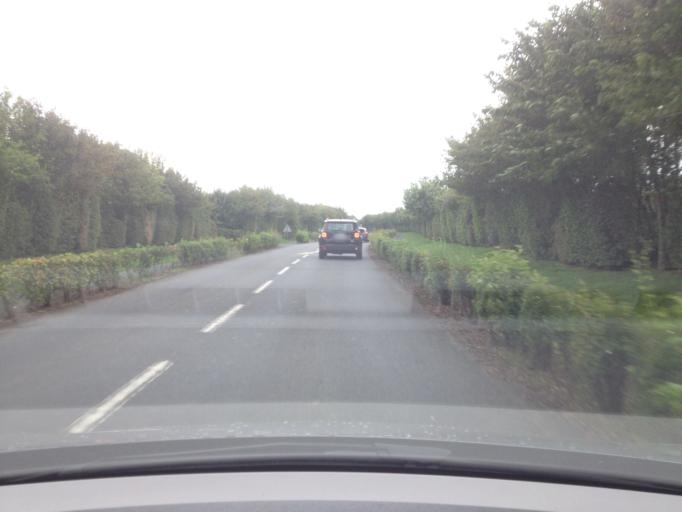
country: FR
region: Lower Normandy
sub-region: Departement du Calvados
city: Grandcamp-Maisy
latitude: 49.3899
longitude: -0.9910
